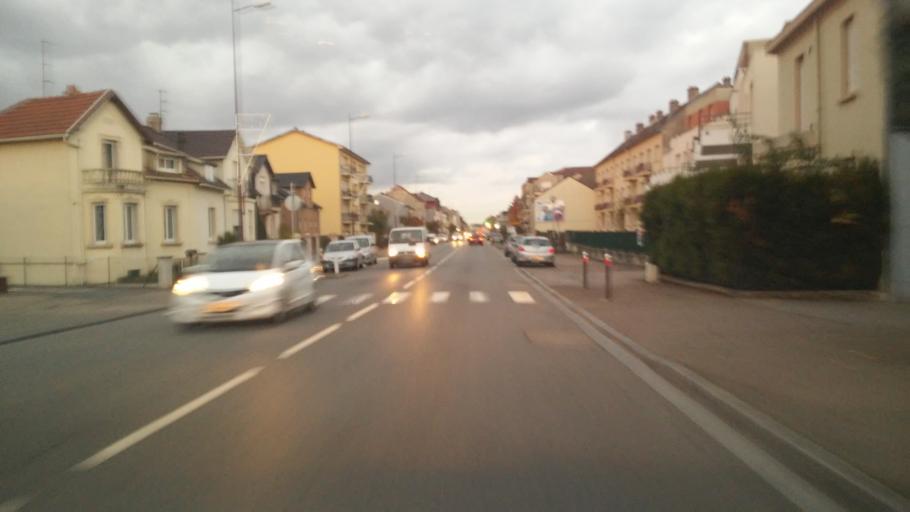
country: FR
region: Lorraine
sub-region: Departement de la Moselle
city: Talange
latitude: 49.2327
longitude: 6.1679
